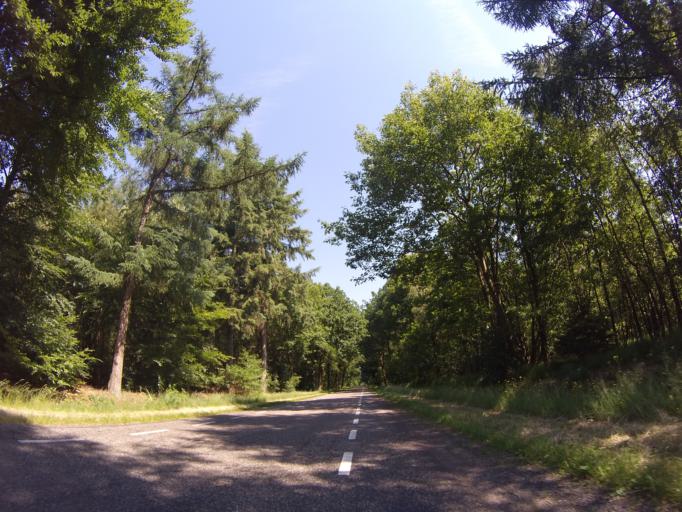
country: NL
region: Drenthe
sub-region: Gemeente Coevorden
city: Sleen
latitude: 52.8222
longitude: 6.7436
